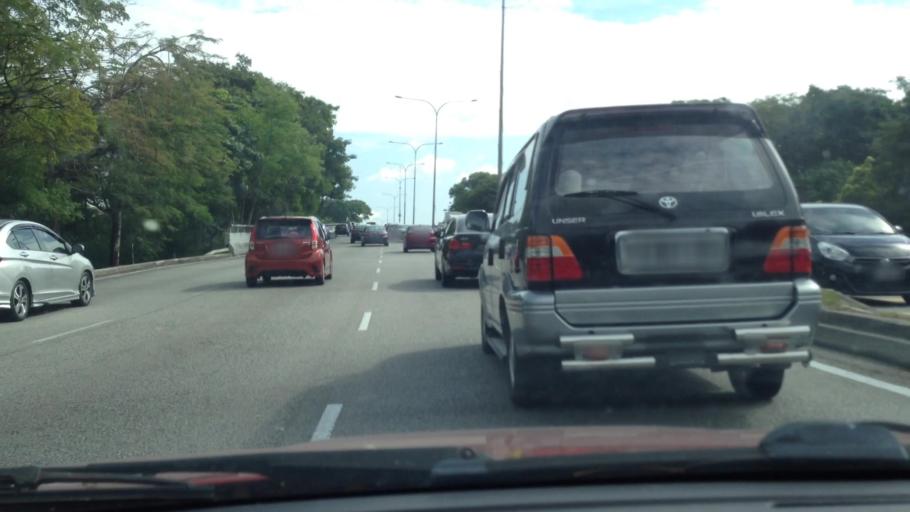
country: MY
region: Selangor
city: Subang Jaya
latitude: 3.0610
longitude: 101.5802
